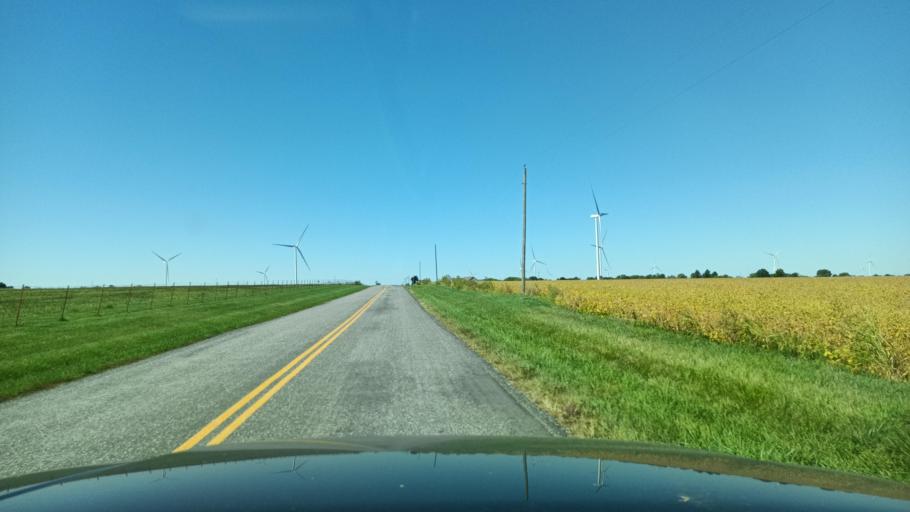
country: US
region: Missouri
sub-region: Adair County
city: Kirksville
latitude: 40.3307
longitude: -92.4718
